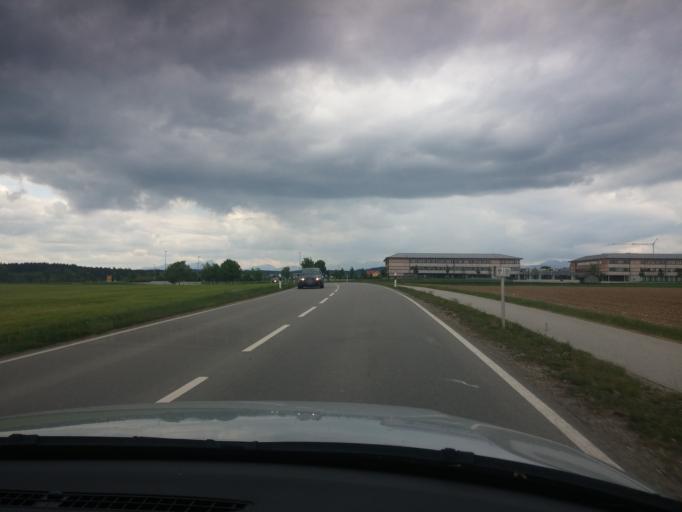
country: DE
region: Bavaria
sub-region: Upper Bavaria
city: Holzkirchen
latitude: 47.8913
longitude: 11.7026
